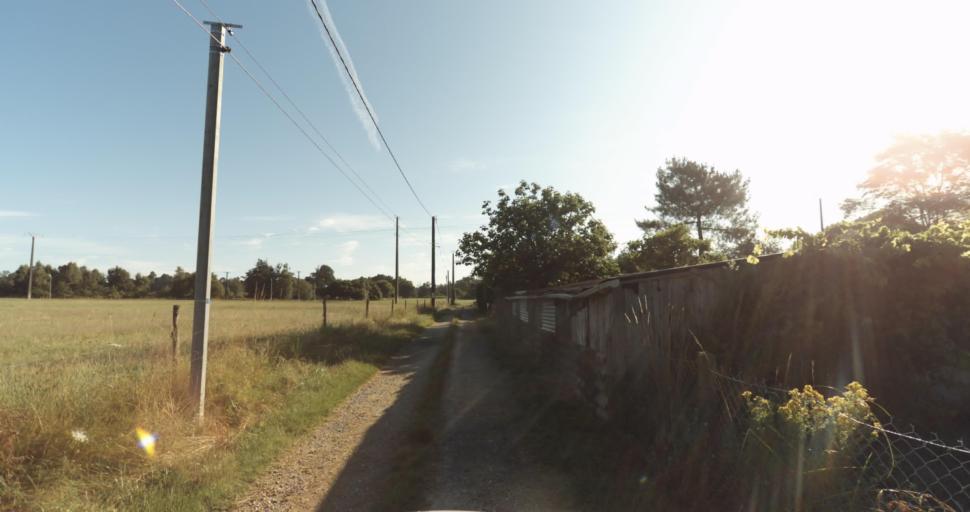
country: FR
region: Aquitaine
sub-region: Departement de la Gironde
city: Bazas
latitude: 44.4082
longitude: -0.2140
